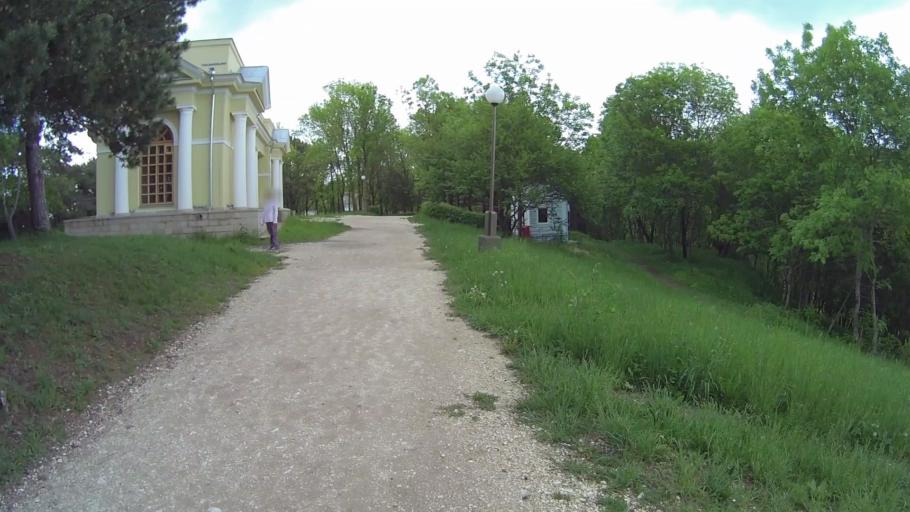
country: RU
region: Stavropol'skiy
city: Kislovodsk
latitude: 43.8968
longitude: 42.7366
